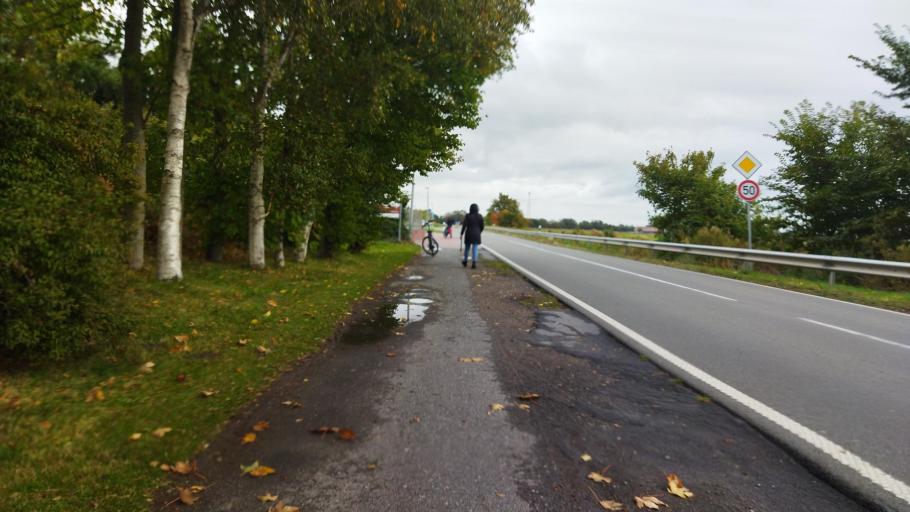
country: DE
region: Lower Saxony
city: Wirdum
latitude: 53.4955
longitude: 7.1045
